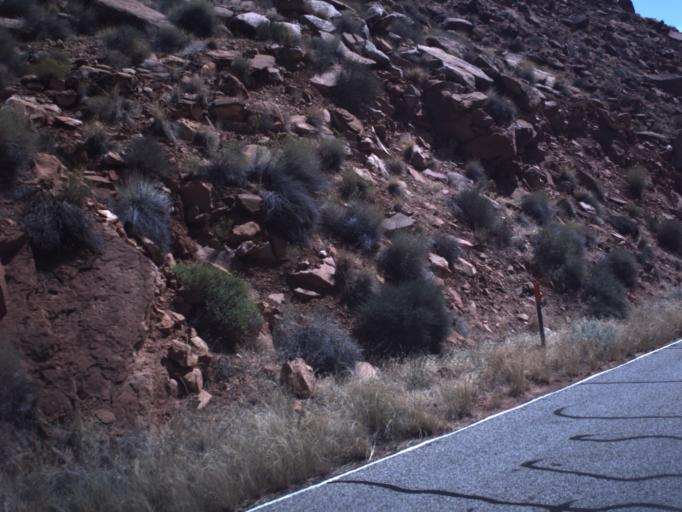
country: US
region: Utah
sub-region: Grand County
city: Moab
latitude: 38.7812
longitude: -109.3320
